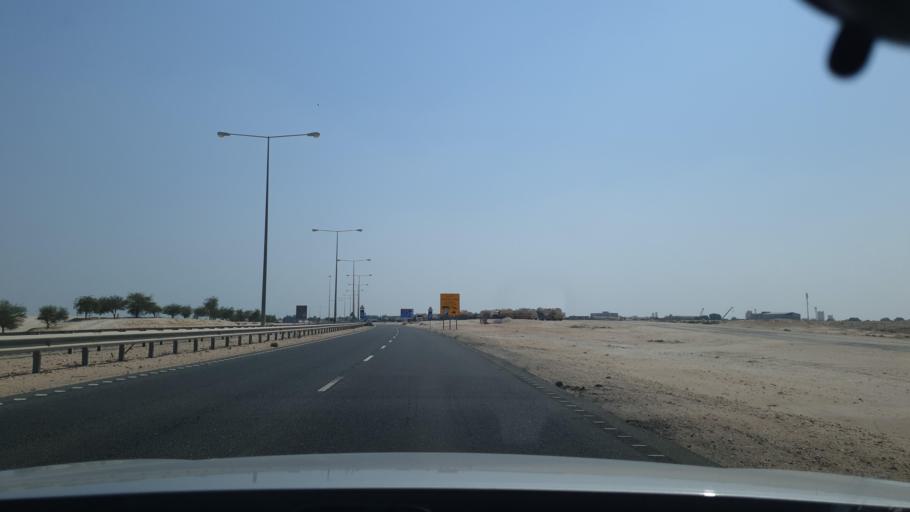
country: QA
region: Al Khawr
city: Al Khawr
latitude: 25.7248
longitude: 51.4973
